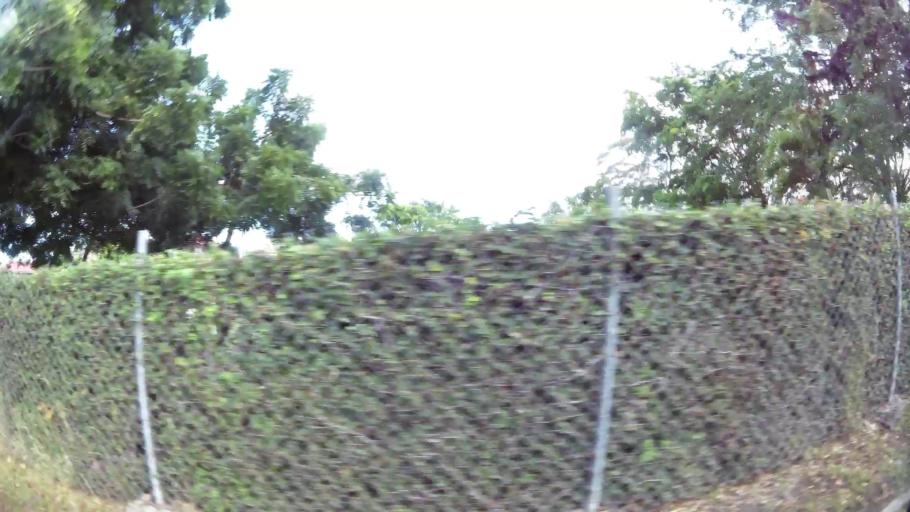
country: KN
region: Saint Paul Charlestown
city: Charlestown
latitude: 17.1316
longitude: -62.6232
